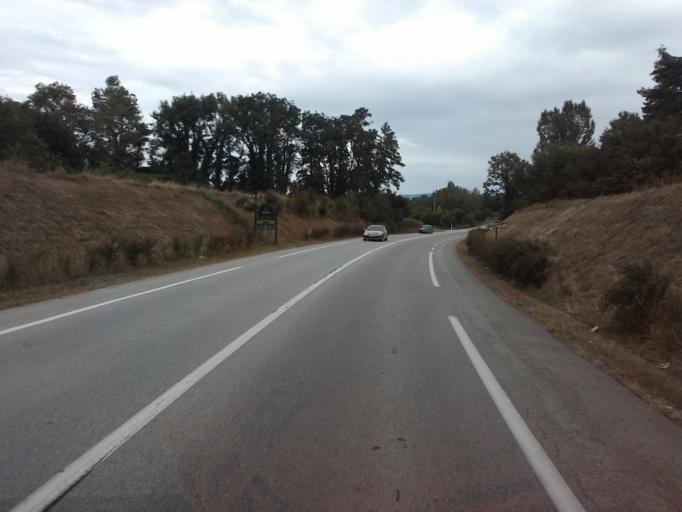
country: FR
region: Rhone-Alpes
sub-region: Departement de l'Isere
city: Morestel
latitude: 45.6829
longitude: 5.4585
